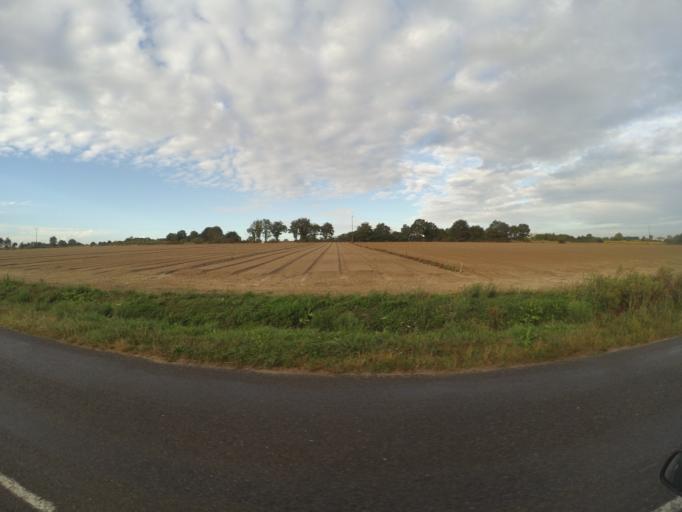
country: FR
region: Pays de la Loire
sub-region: Departement de la Loire-Atlantique
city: La Planche
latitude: 47.0222
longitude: -1.4607
